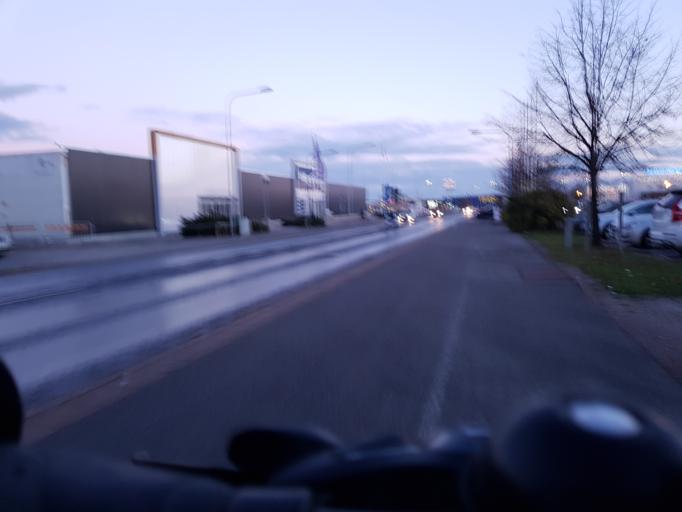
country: SE
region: Uppsala
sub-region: Uppsala Kommun
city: Saevja
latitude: 59.8516
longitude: 17.6880
